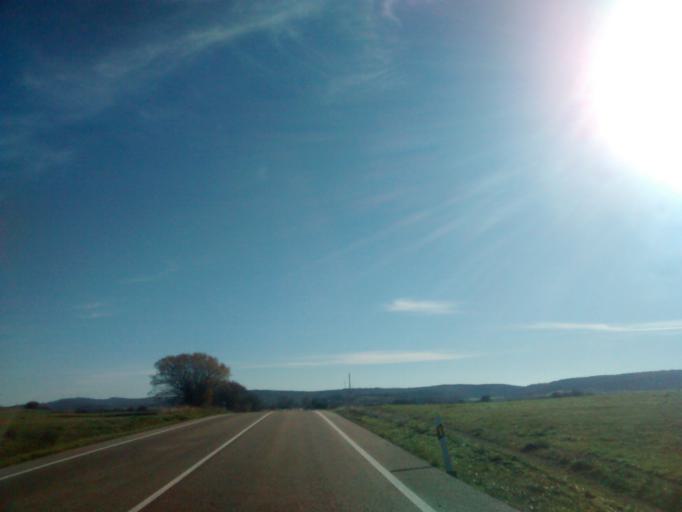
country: ES
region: Cantabria
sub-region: Provincia de Cantabria
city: San Pedro del Romeral
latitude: 42.9800
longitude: -3.8068
